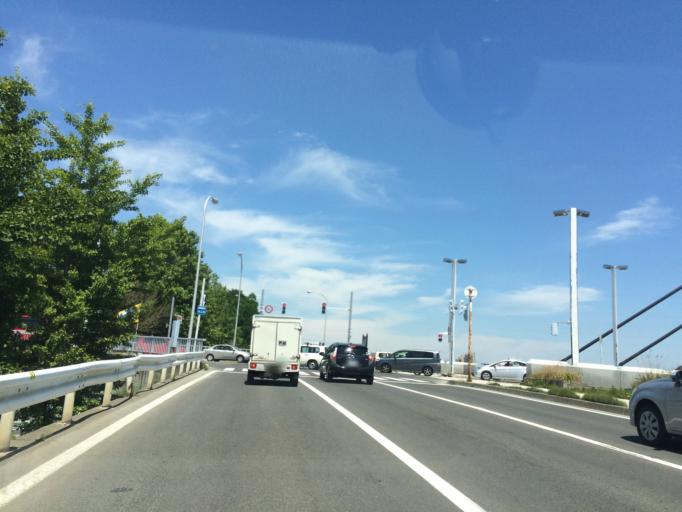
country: JP
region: Hokkaido
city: Sapporo
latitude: 43.0168
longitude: 141.3521
